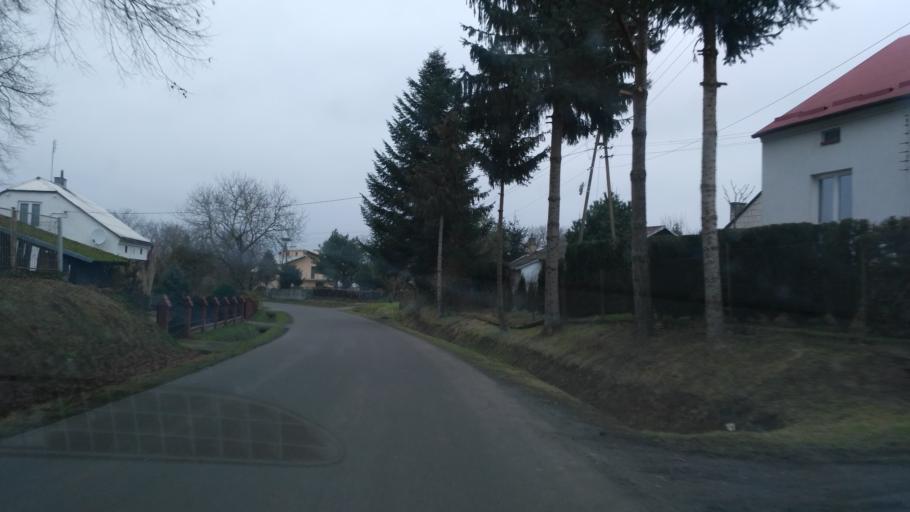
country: PL
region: Subcarpathian Voivodeship
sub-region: Powiat jaroslawski
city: Pruchnik
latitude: 49.9282
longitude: 22.5358
